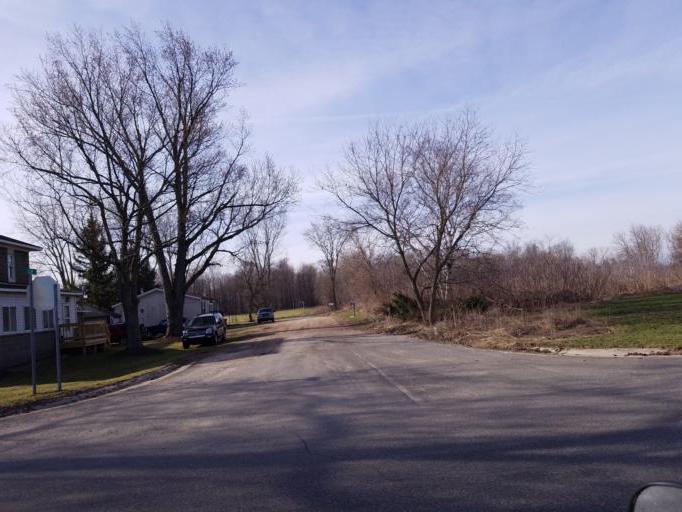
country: US
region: Michigan
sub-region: Montcalm County
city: Howard City
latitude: 43.4316
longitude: -85.3914
